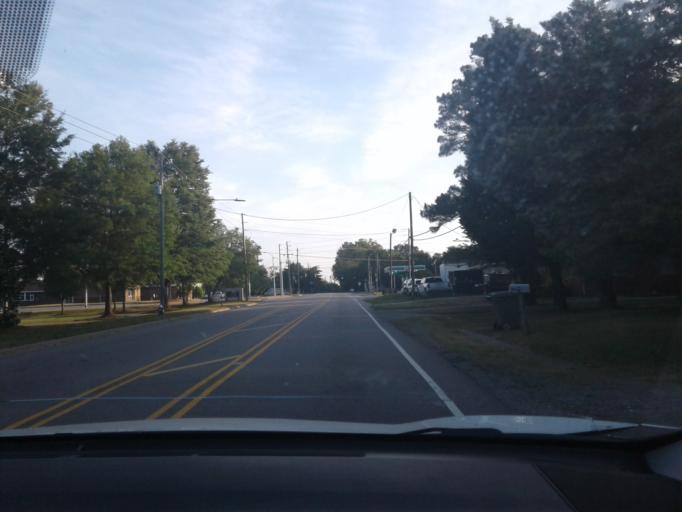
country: US
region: North Carolina
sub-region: Wake County
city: Fuquay-Varina
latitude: 35.5716
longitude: -78.8006
